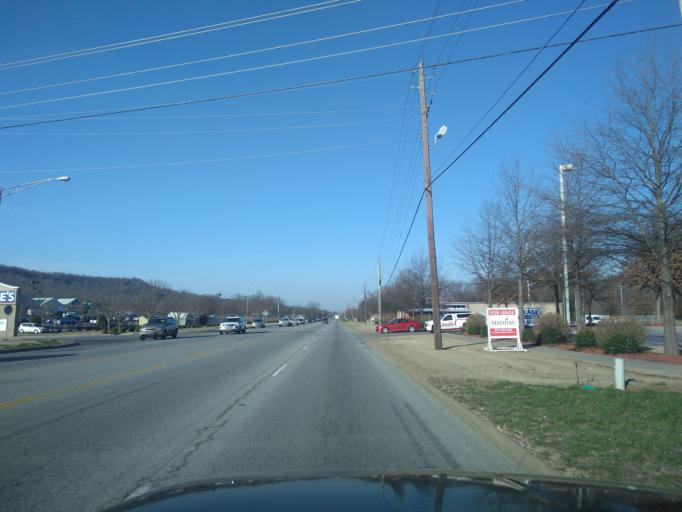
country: US
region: Arkansas
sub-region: Washington County
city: Farmington
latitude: 36.0513
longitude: -94.2049
